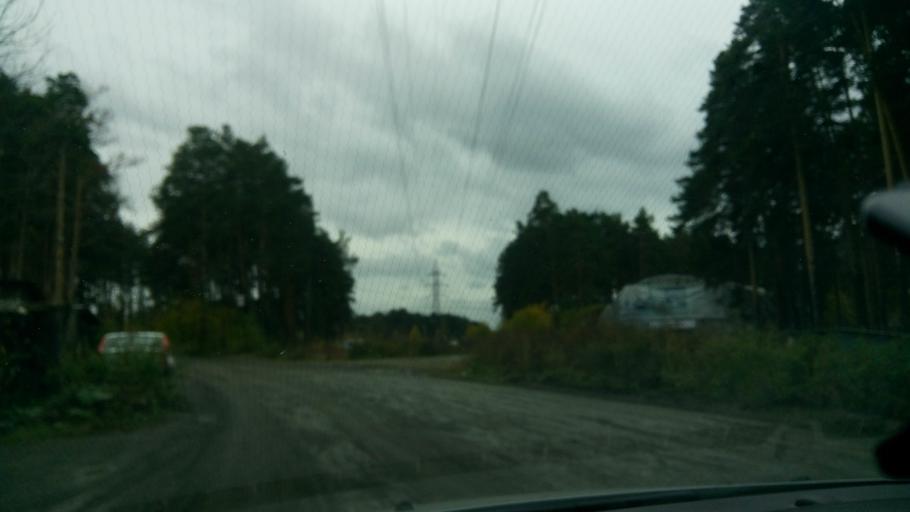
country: RU
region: Sverdlovsk
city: Shirokaya Rechka
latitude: 56.8186
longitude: 60.5229
